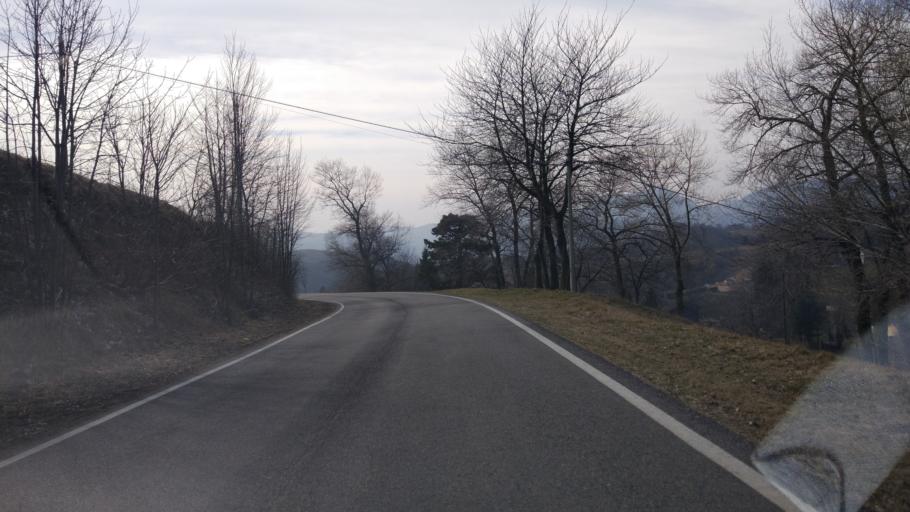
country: IT
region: Veneto
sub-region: Provincia di Verona
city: Selva di Progno
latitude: 45.6335
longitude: 11.1586
